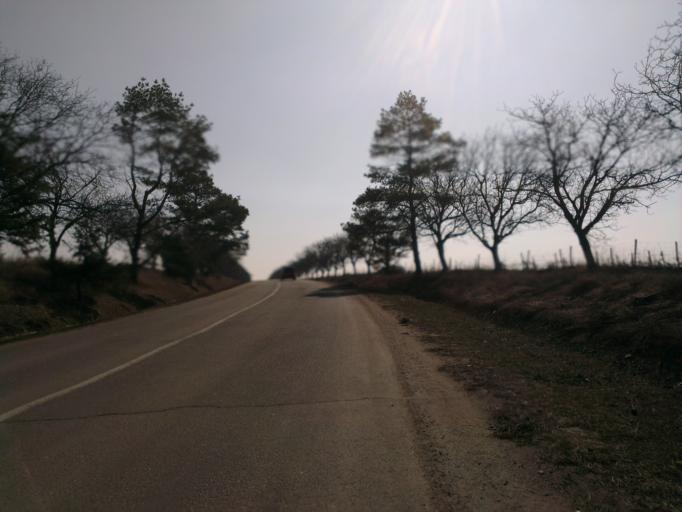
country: MD
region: Chisinau
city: Cricova
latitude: 47.1300
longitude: 28.8531
